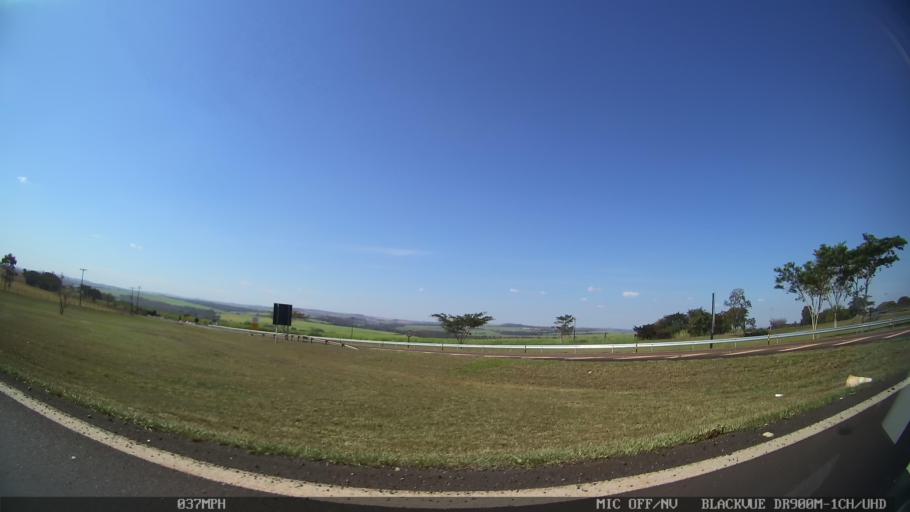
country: BR
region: Sao Paulo
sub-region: Jardinopolis
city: Jardinopolis
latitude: -21.0907
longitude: -47.7936
